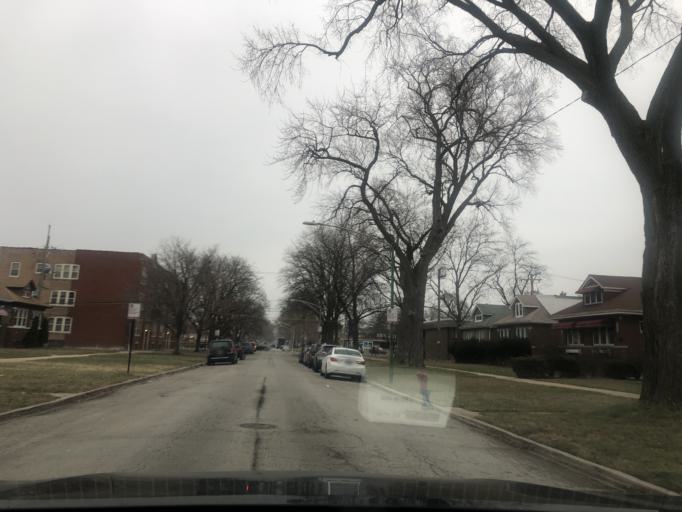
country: US
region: Illinois
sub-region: Cook County
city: Evergreen Park
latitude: 41.7497
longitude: -87.6214
